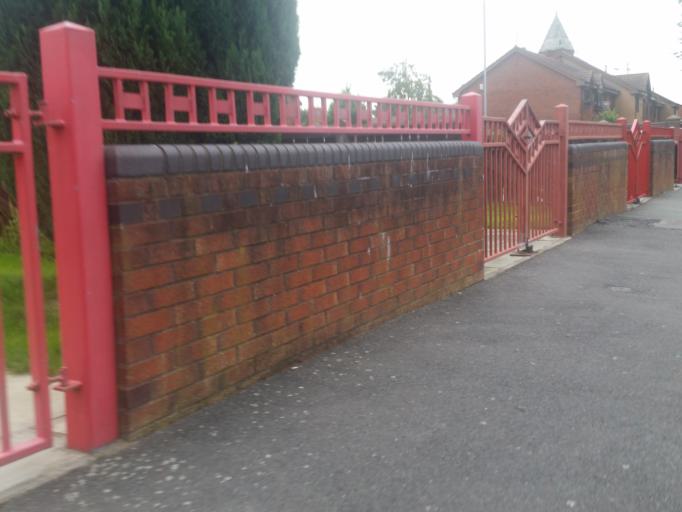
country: GB
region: England
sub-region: City and Borough of Salford
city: Salford
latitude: 53.4762
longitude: -2.2773
